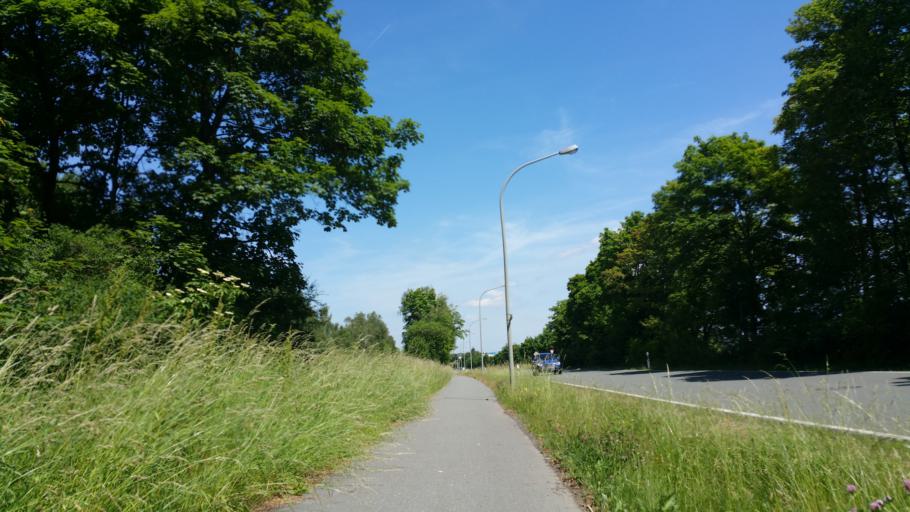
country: DE
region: Bavaria
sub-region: Upper Franconia
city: Schwarzenbach an der Saale
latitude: 50.2191
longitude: 11.9526
